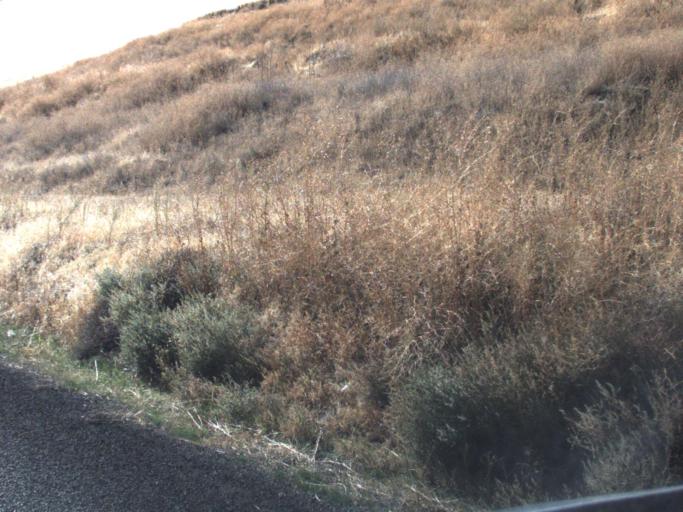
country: US
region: Washington
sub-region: Walla Walla County
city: Waitsburg
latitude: 46.2840
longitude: -118.3416
